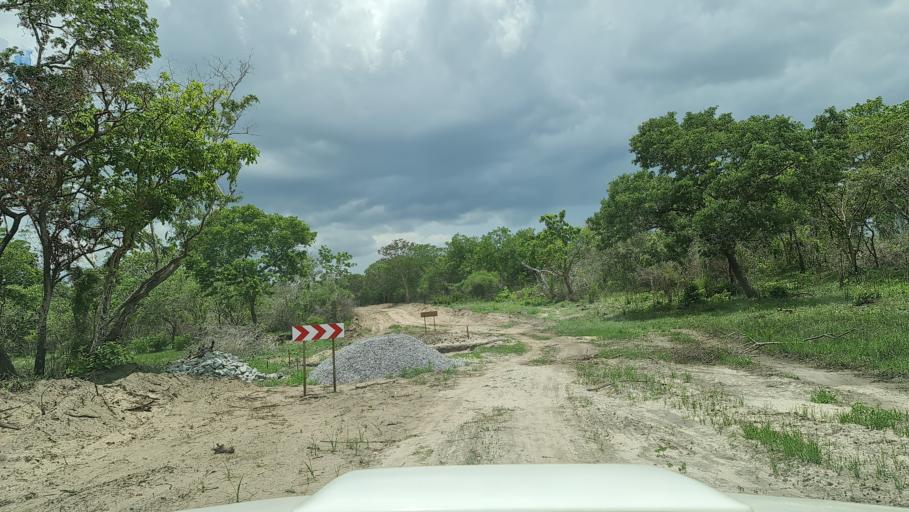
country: MZ
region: Nampula
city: Ilha de Mocambique
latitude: -15.2445
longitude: 40.3648
